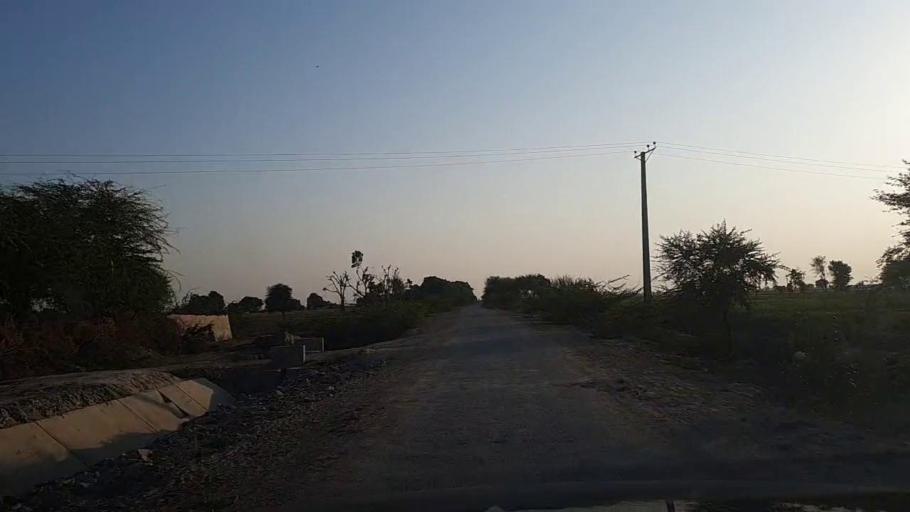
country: PK
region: Sindh
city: Naukot
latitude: 24.8443
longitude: 69.3136
